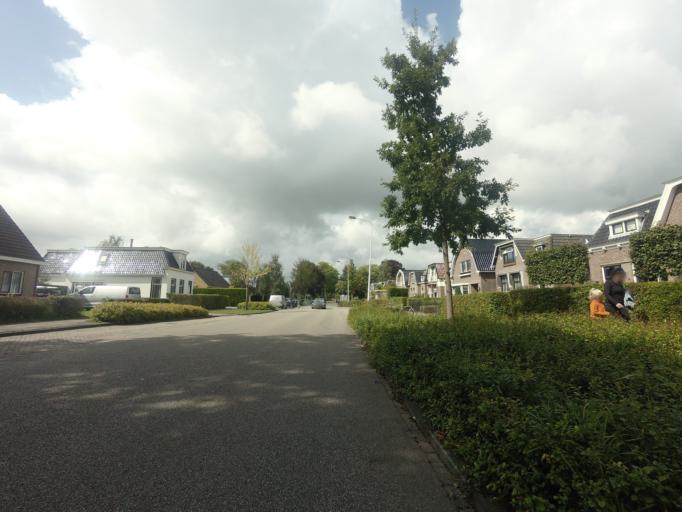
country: NL
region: Friesland
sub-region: Gemeente Skarsterlan
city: Joure
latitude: 52.9622
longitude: 5.8072
